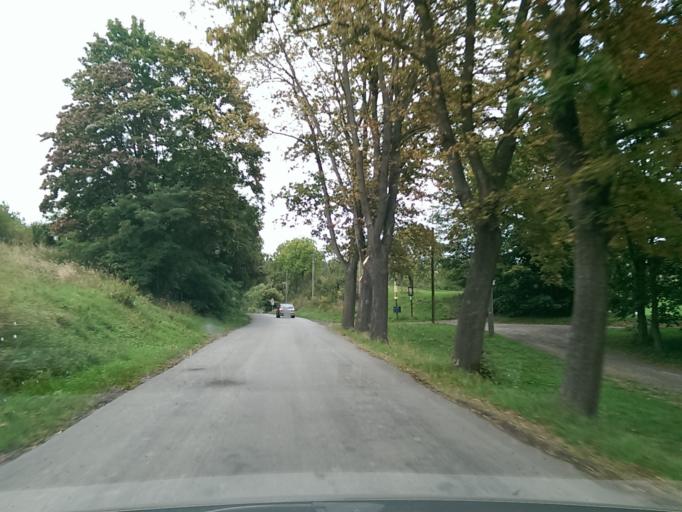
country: CZ
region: Central Bohemia
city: Knezmost
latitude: 50.5117
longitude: 15.0232
